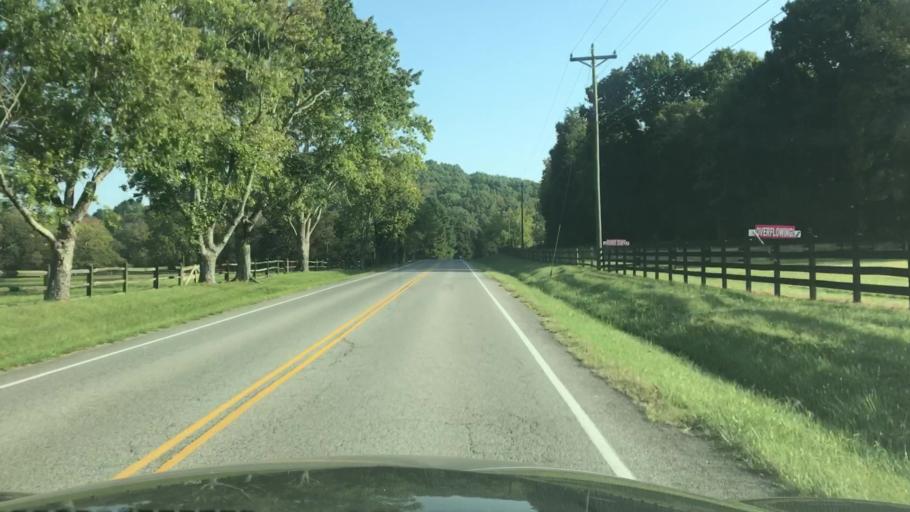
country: US
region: Tennessee
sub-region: Davidson County
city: Forest Hills
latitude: 36.0331
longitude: -86.9153
